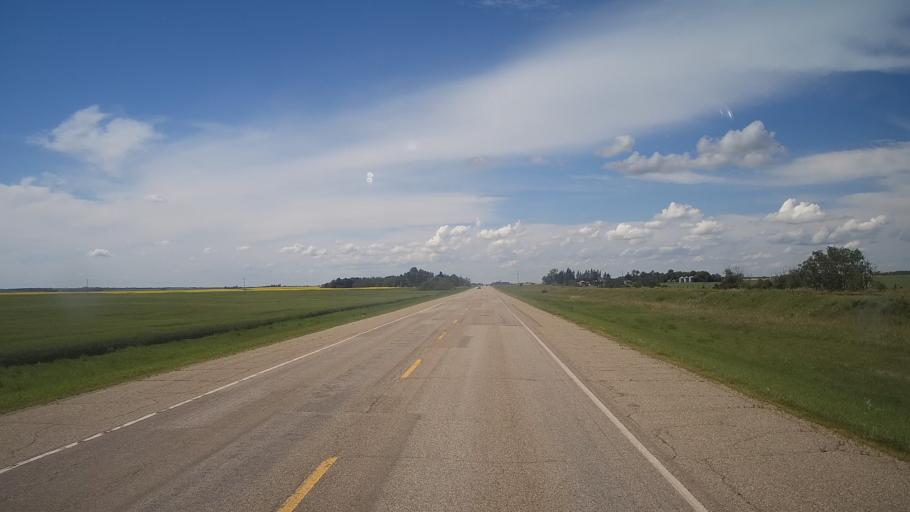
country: CA
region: Saskatchewan
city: Yorkton
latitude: 51.0870
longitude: -102.2558
